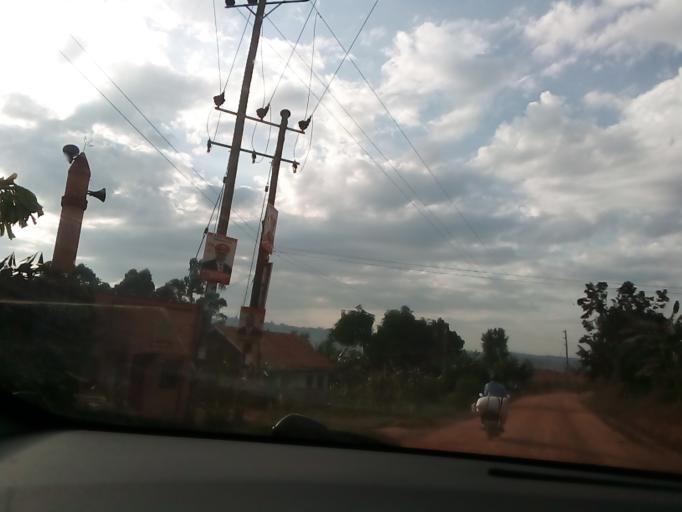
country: UG
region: Central Region
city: Masaka
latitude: -0.3508
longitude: 31.7185
